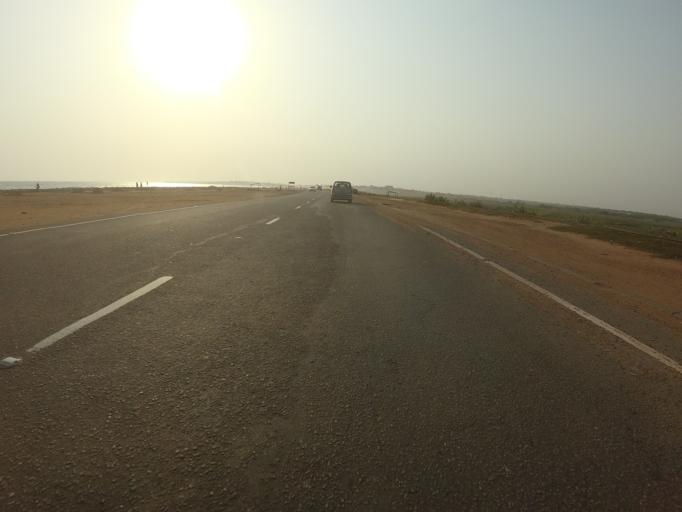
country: GH
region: Greater Accra
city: Nungua
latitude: 5.6137
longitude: -0.0331
